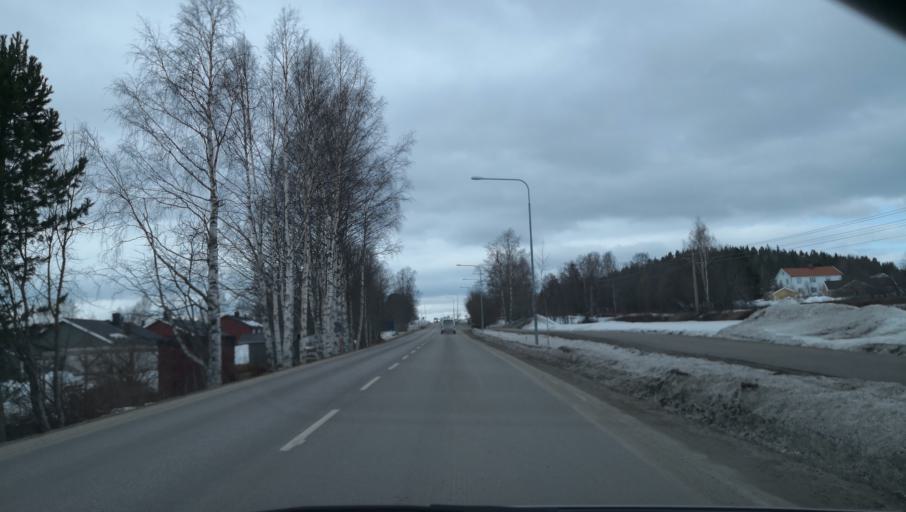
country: SE
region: Vaesterbotten
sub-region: Vannas Kommun
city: Vannasby
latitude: 63.9145
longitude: 19.8106
